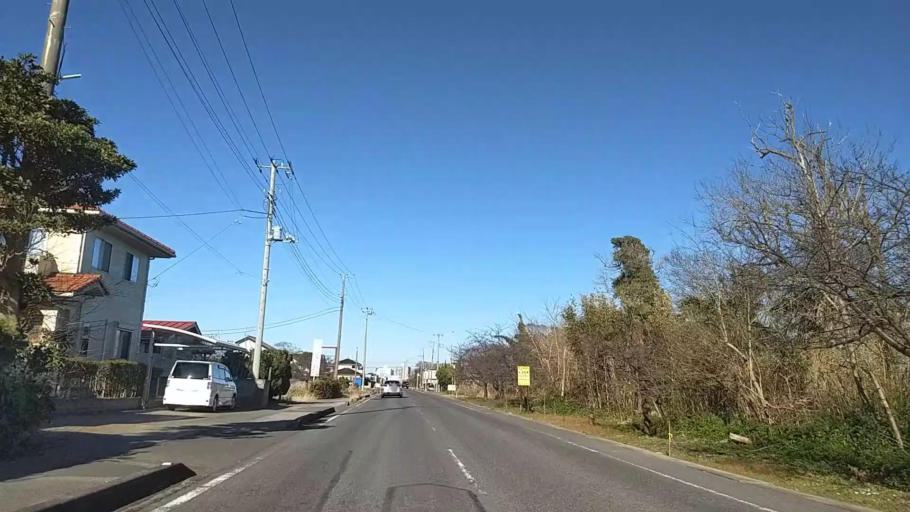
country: JP
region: Chiba
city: Mobara
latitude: 35.4382
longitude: 140.3986
